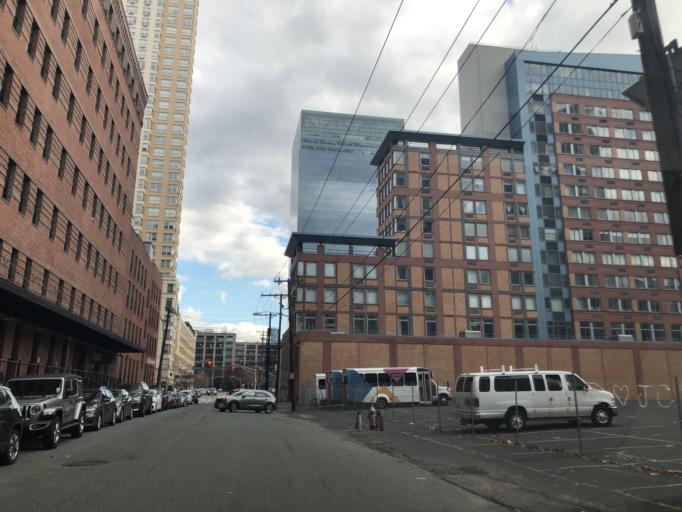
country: US
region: New Jersey
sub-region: Hudson County
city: Hoboken
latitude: 40.7197
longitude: -74.0381
